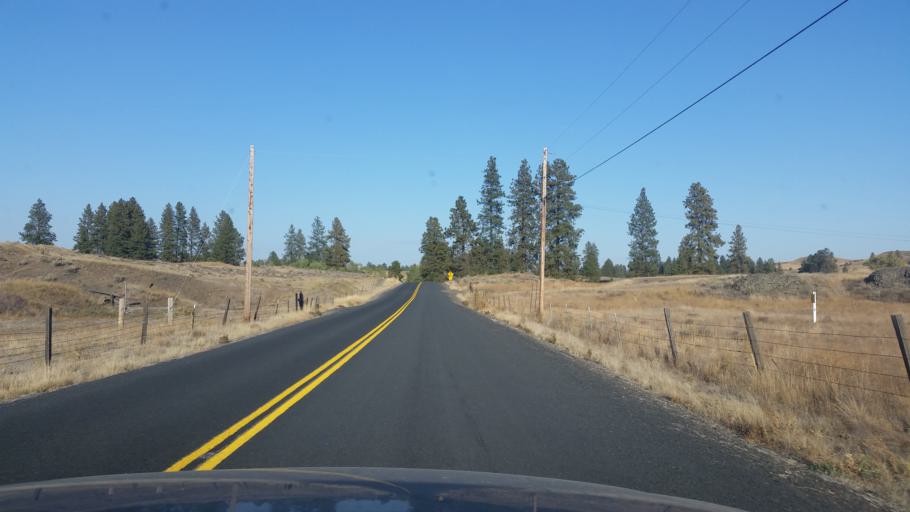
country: US
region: Washington
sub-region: Spokane County
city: Cheney
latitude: 47.3433
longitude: -117.7295
